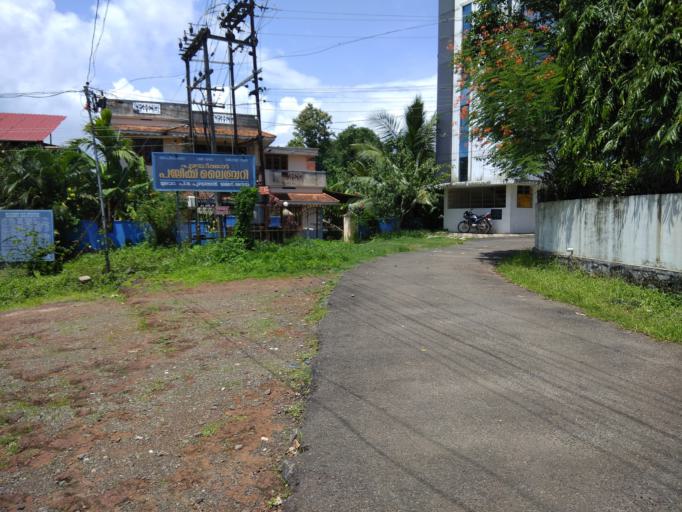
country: IN
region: Kerala
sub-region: Thrissur District
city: Trichur
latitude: 10.5522
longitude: 76.1753
